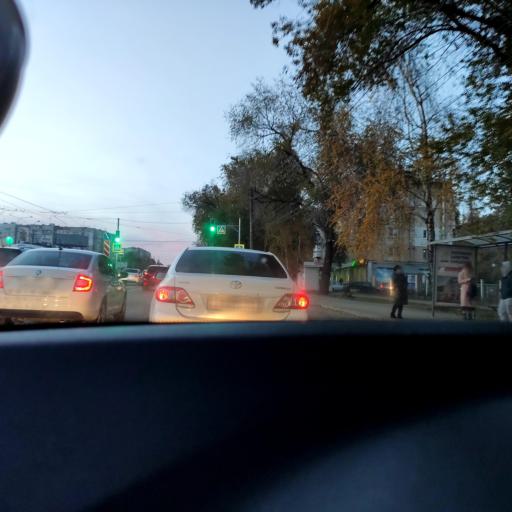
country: RU
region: Samara
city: Samara
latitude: 53.2115
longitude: 50.2293
